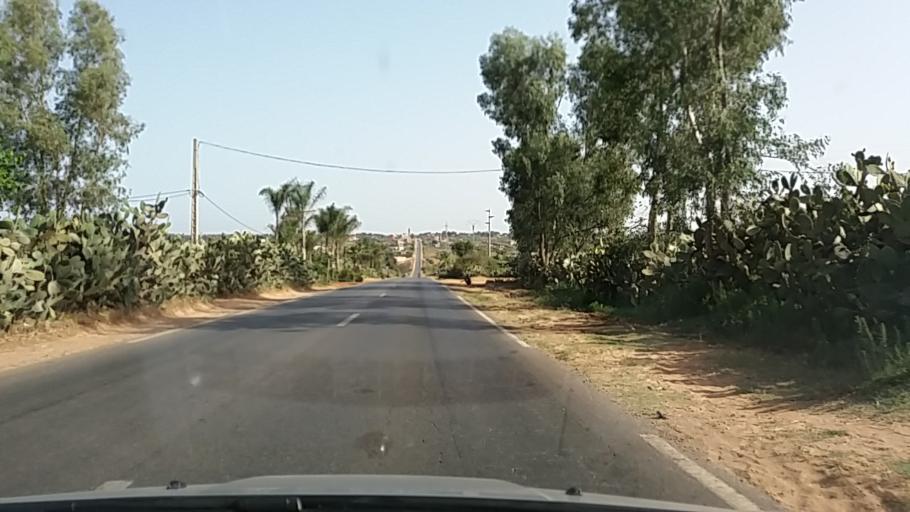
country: MA
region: Gharb-Chrarda-Beni Hssen
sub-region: Kenitra Province
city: Kenitra
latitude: 34.1114
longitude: -6.5591
